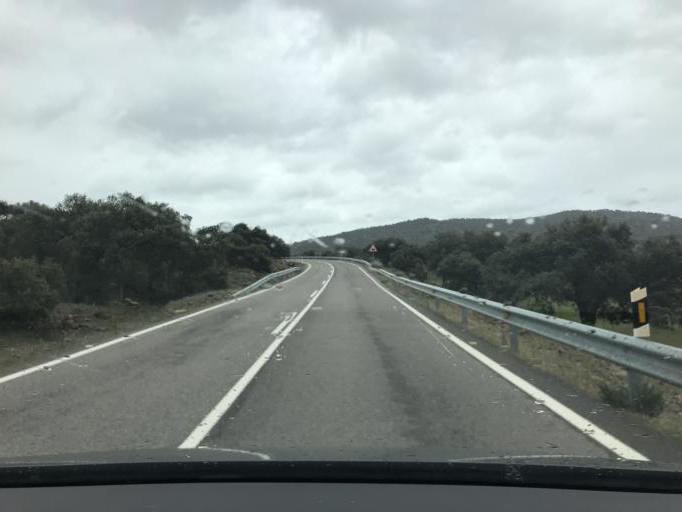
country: ES
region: Andalusia
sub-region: Province of Cordoba
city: Fuente Obejuna
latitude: 38.1521
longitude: -5.5132
